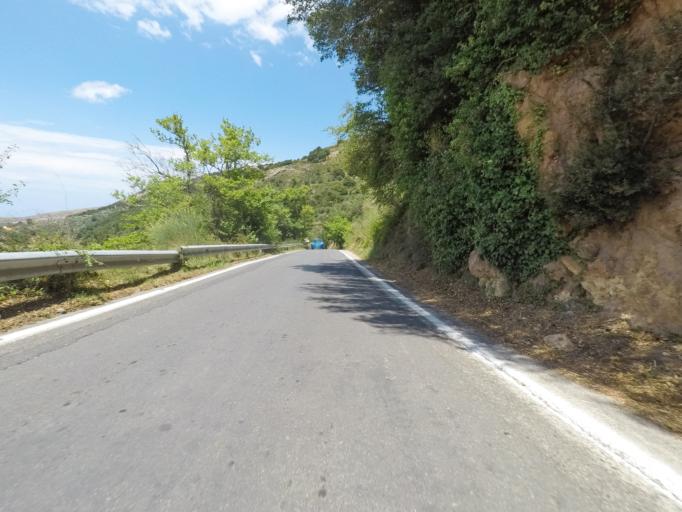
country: GR
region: Crete
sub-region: Nomos Irakleiou
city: Mokhos
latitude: 35.2204
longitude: 25.4616
